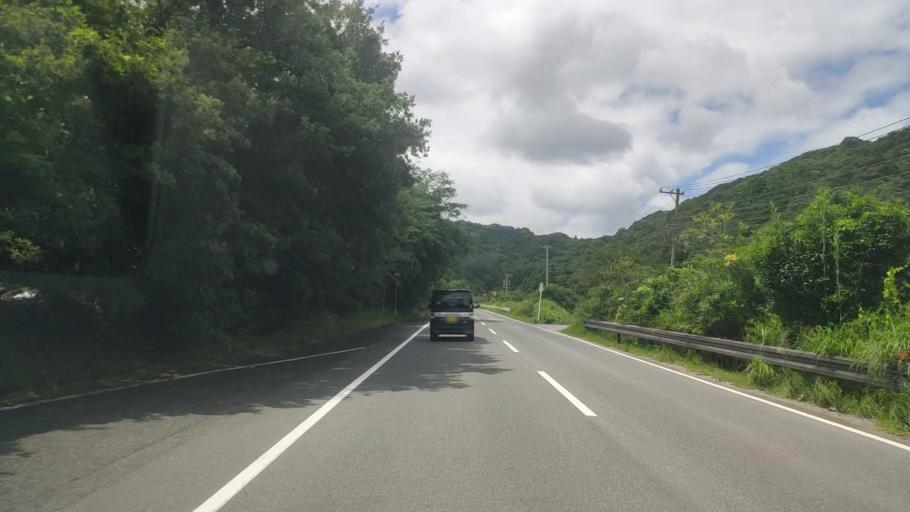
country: JP
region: Mie
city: Toba
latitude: 34.4194
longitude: 136.8169
